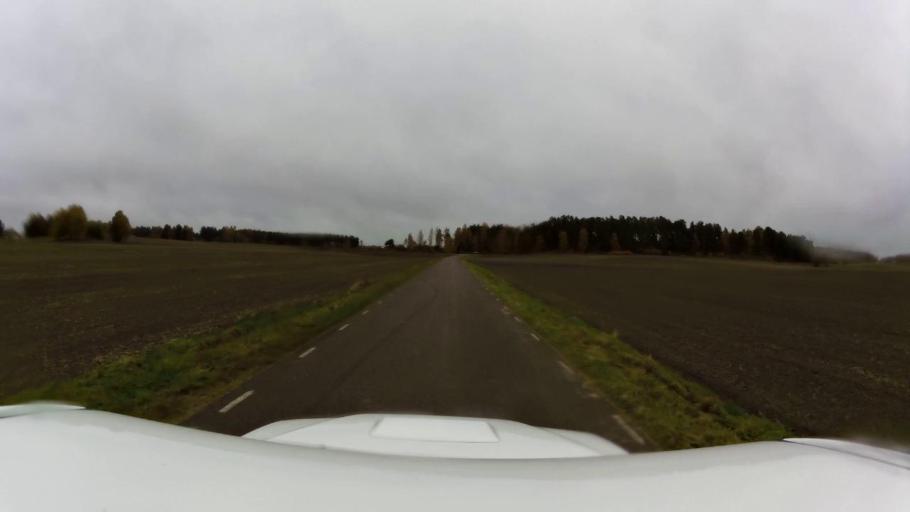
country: SE
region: OEstergoetland
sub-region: Norrkopings Kommun
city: Kimstad
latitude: 58.3953
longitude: 15.9508
